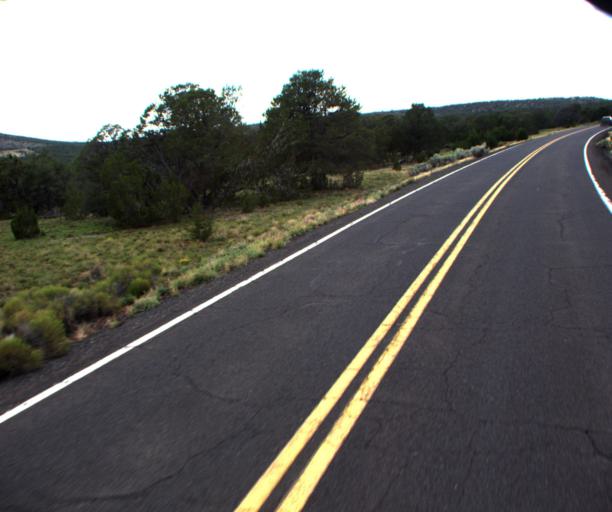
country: US
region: Arizona
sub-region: Coconino County
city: Parks
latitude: 35.5325
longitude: -111.8497
